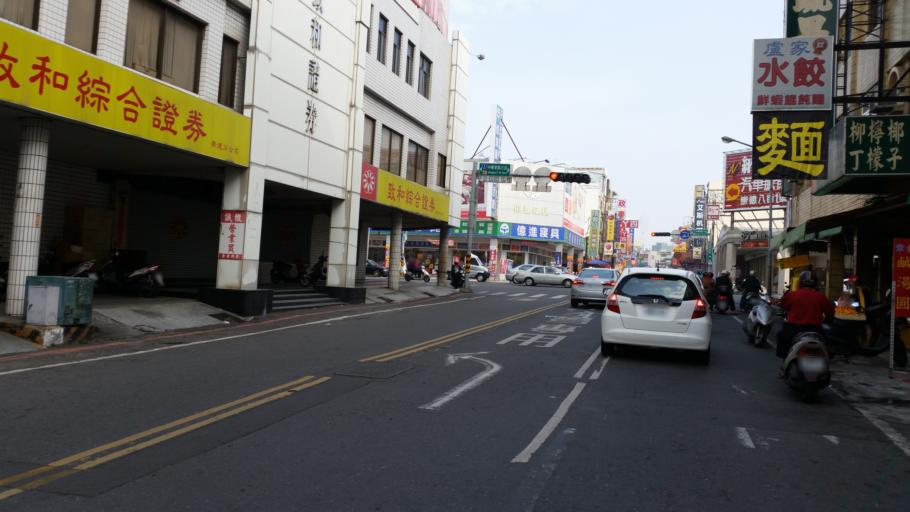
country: TW
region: Taiwan
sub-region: Tainan
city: Tainan
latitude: 22.9762
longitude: 120.2243
